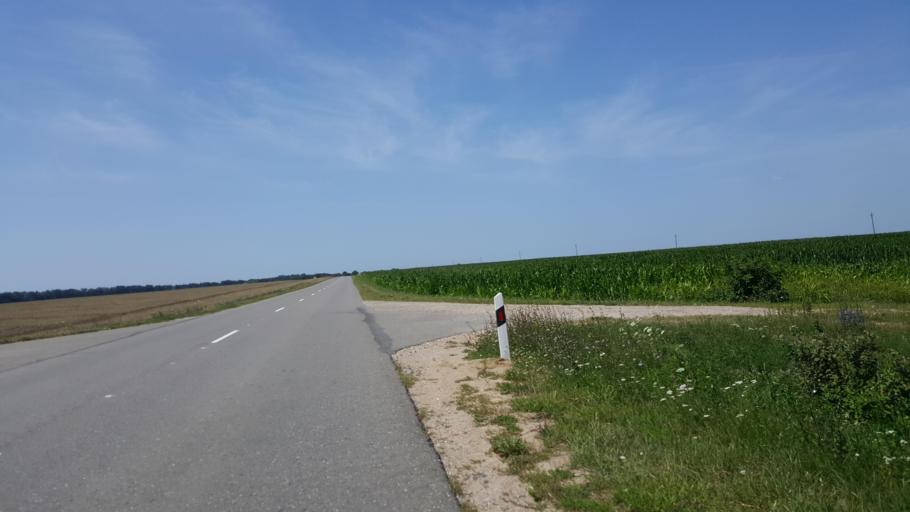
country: BY
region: Brest
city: Vysokaye
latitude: 52.3520
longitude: 23.4831
